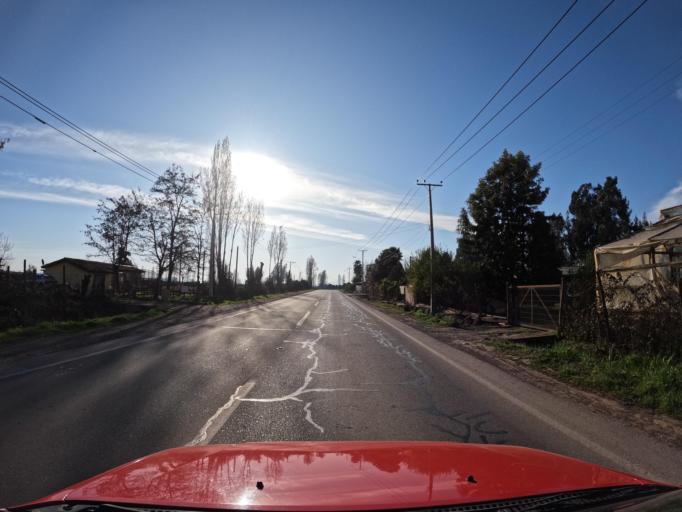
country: CL
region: Maule
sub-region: Provincia de Curico
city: Teno
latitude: -34.9037
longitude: -71.0537
